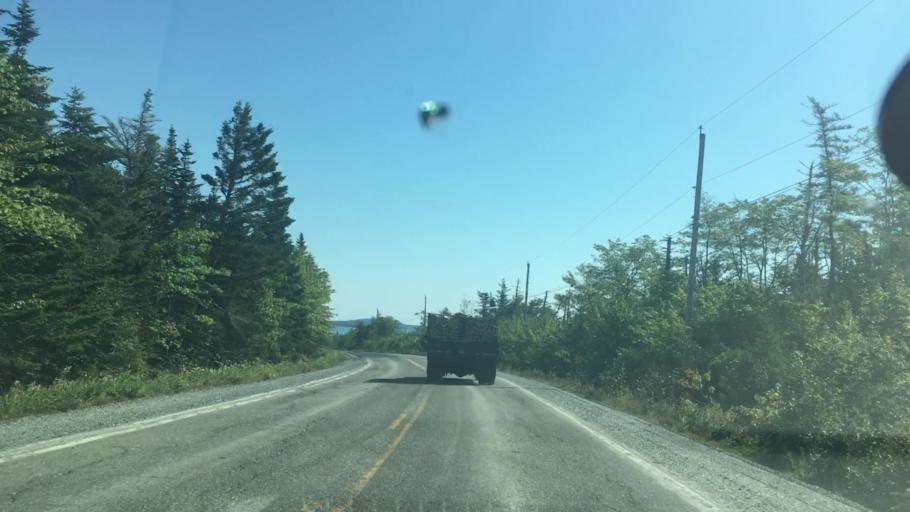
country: CA
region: Nova Scotia
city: New Glasgow
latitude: 44.8983
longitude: -62.4317
